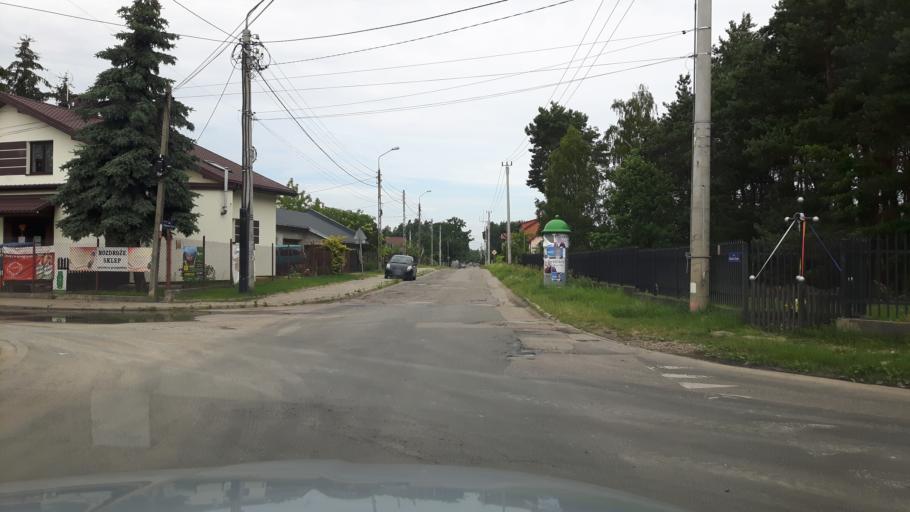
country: PL
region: Masovian Voivodeship
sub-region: Powiat wolominski
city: Wolomin
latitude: 52.3194
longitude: 21.2210
